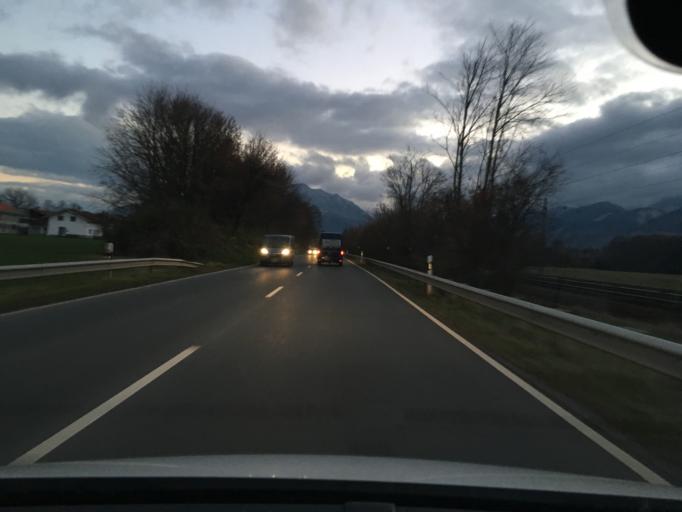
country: DE
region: Bavaria
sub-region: Upper Bavaria
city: Raubling
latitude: 47.7791
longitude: 12.1051
